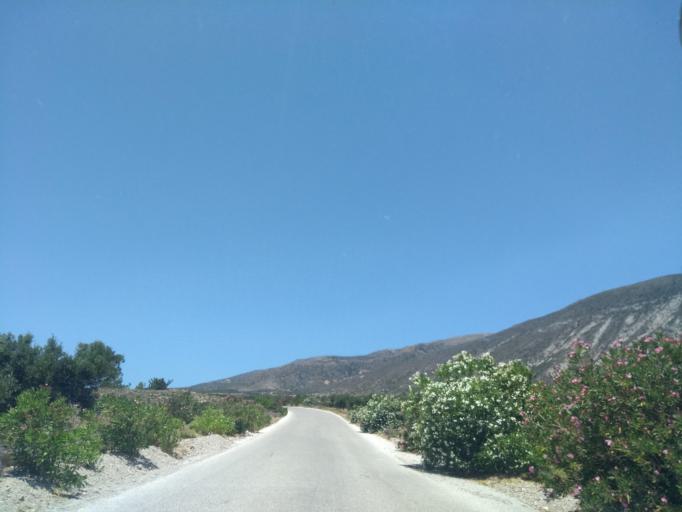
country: GR
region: Crete
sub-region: Nomos Chanias
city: Vryses
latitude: 35.3346
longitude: 23.5454
